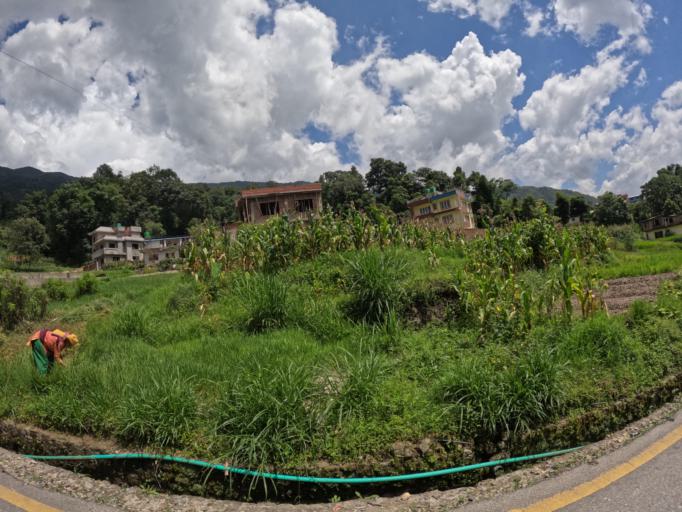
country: NP
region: Central Region
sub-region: Bagmati Zone
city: Kathmandu
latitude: 27.7989
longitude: 85.3299
